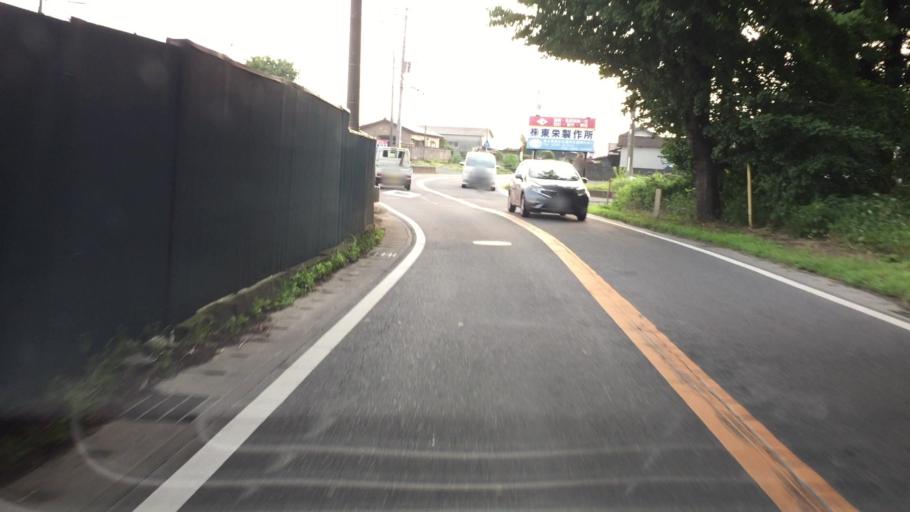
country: JP
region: Tochigi
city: Fujioka
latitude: 36.2613
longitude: 139.6443
